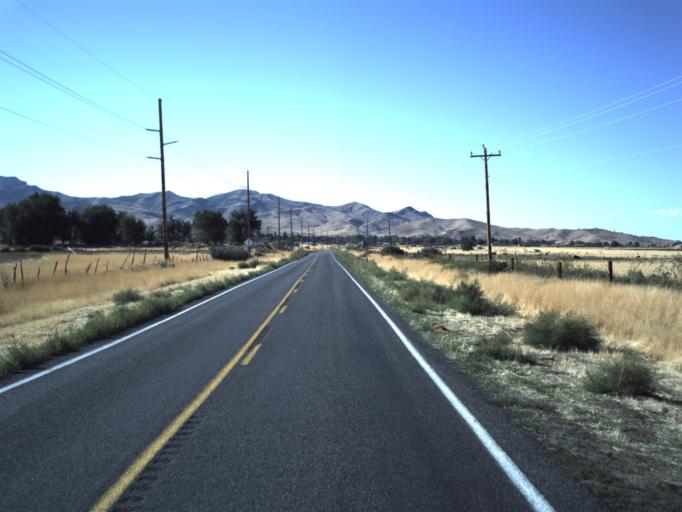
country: US
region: Utah
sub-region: Millard County
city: Delta
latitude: 39.3982
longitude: -112.3355
